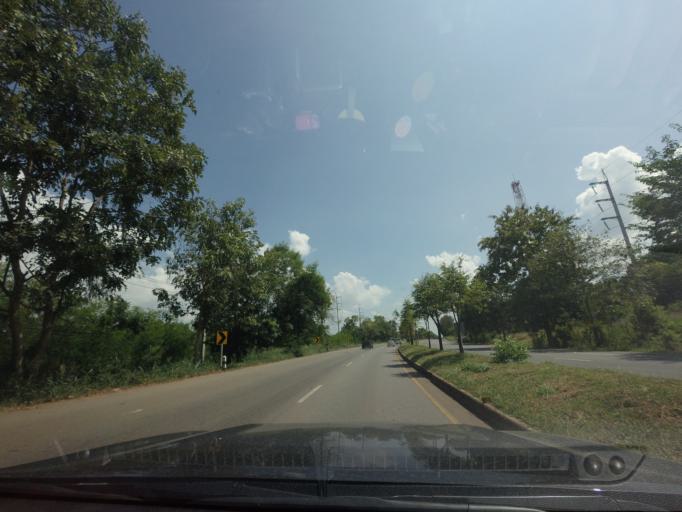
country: TH
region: Phetchabun
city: Nong Phai
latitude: 16.0754
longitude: 101.0659
